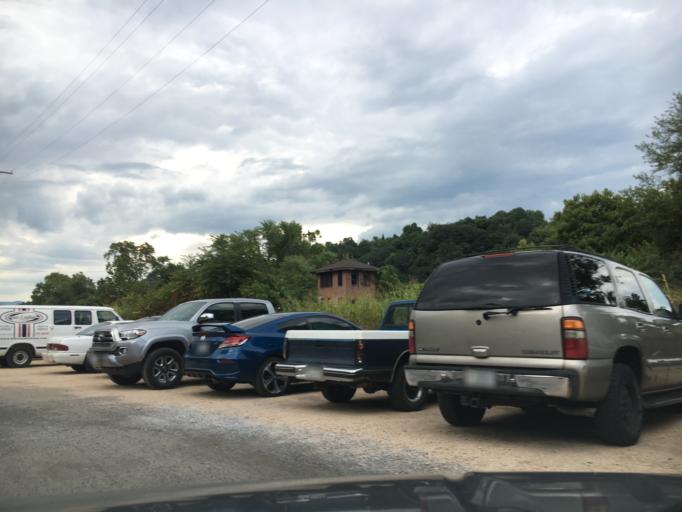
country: US
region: Virginia
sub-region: City of Lynchburg
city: Lynchburg
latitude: 37.4122
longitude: -79.1370
